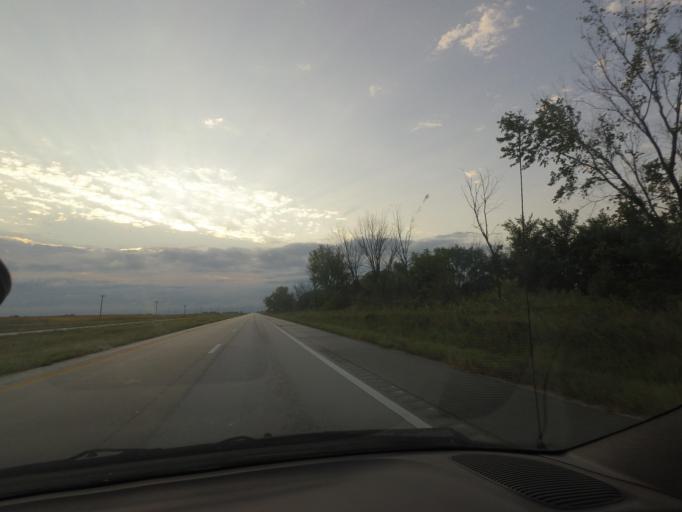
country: US
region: Missouri
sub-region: Shelby County
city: Shelbina
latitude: 39.7158
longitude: -92.1346
